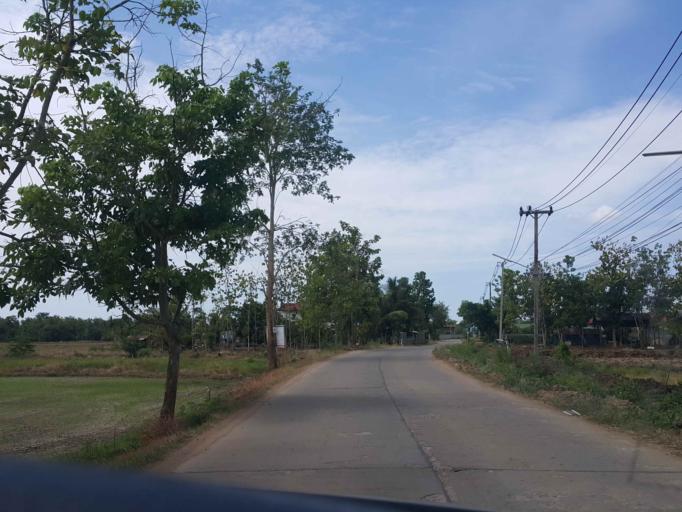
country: TH
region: Sukhothai
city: Thung Saliam
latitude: 17.3339
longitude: 99.5654
